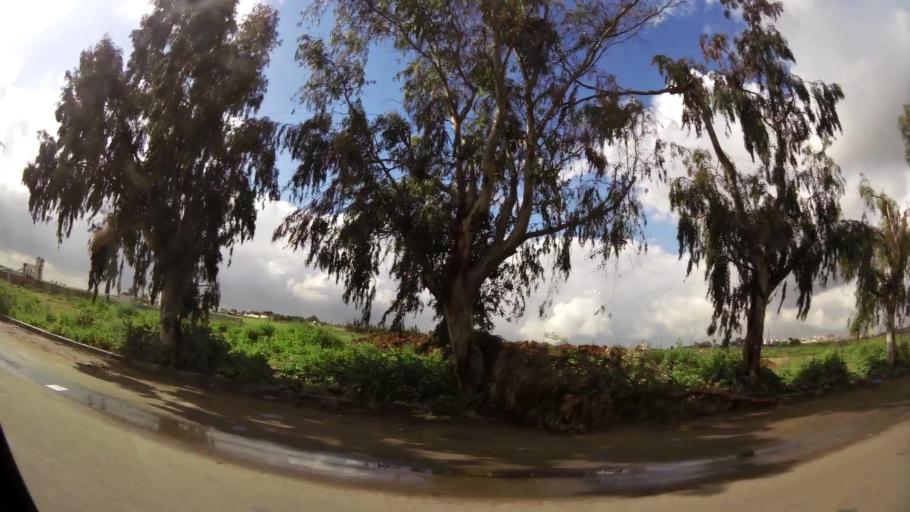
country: MA
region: Grand Casablanca
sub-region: Mediouna
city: Tit Mellil
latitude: 33.5673
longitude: -7.5098
